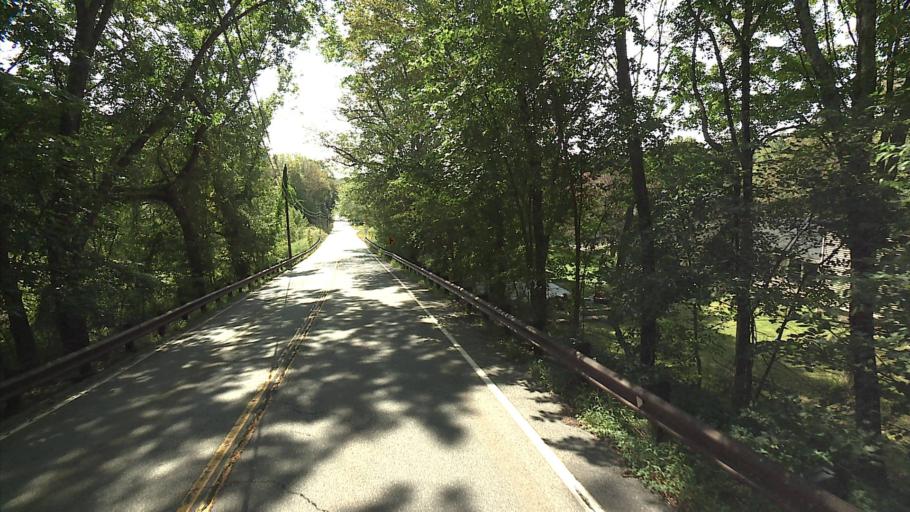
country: US
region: Connecticut
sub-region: Windham County
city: Quinebaug
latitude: 41.9948
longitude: -71.9993
